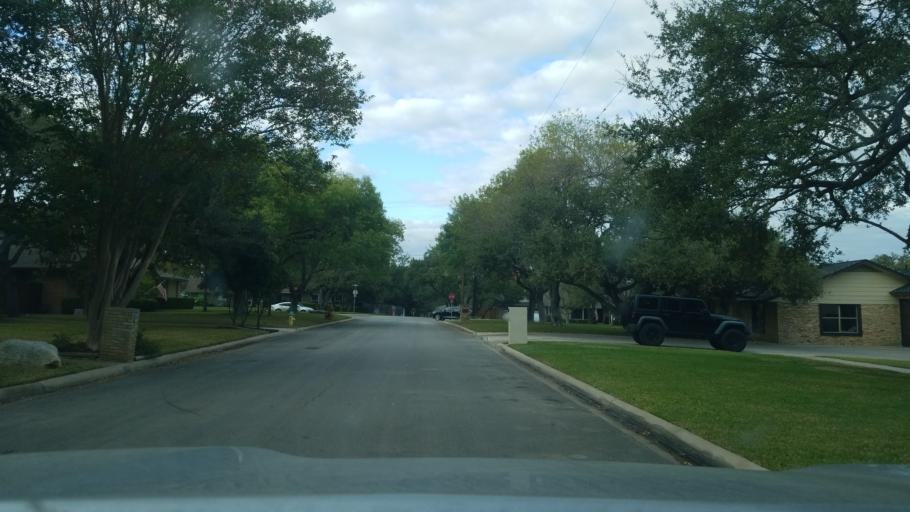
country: US
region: Texas
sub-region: Bexar County
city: Hollywood Park
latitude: 29.6030
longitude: -98.4842
